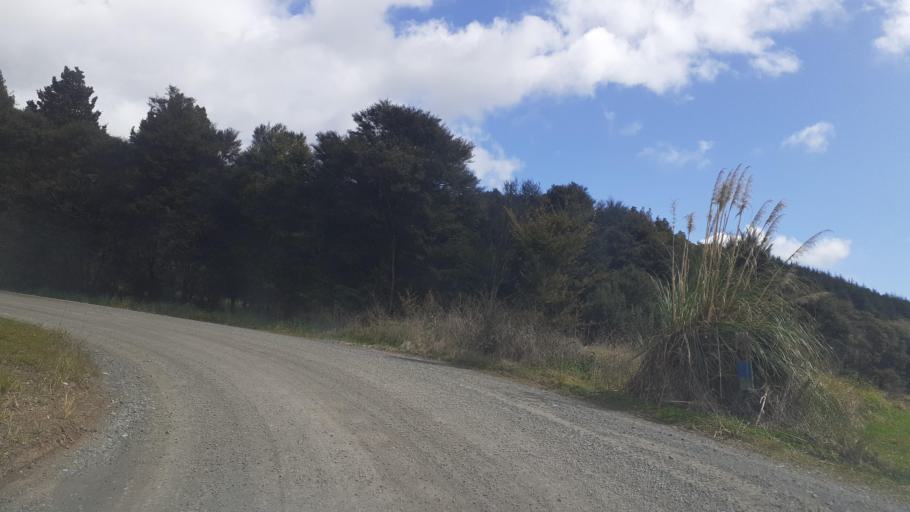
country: NZ
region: Northland
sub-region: Far North District
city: Moerewa
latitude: -35.5787
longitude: 173.9430
